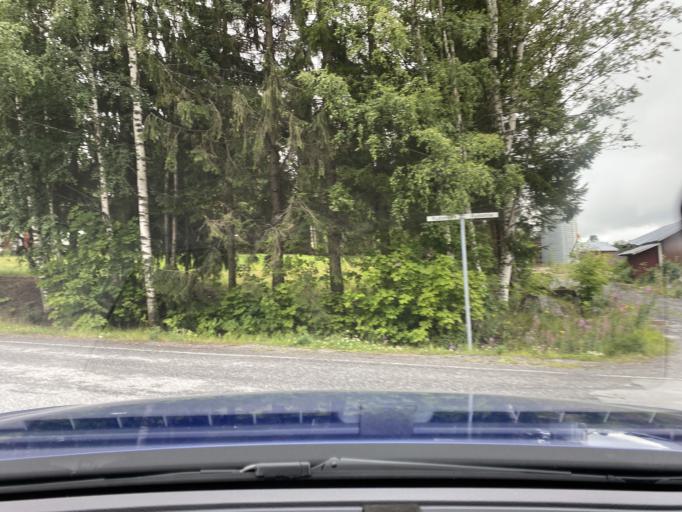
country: FI
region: Ostrobothnia
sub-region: Kyroenmaa
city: Laihia
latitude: 62.9816
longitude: 21.9918
